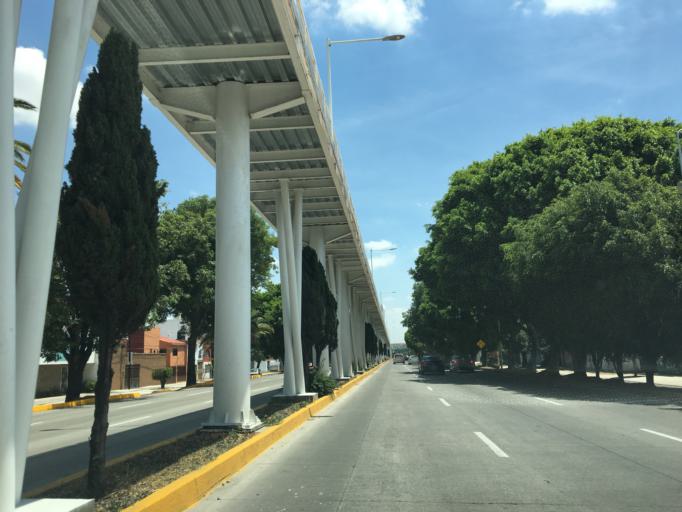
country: MX
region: Puebla
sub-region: Cuautlancingo
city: Sanctorum
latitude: 19.0878
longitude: -98.2291
